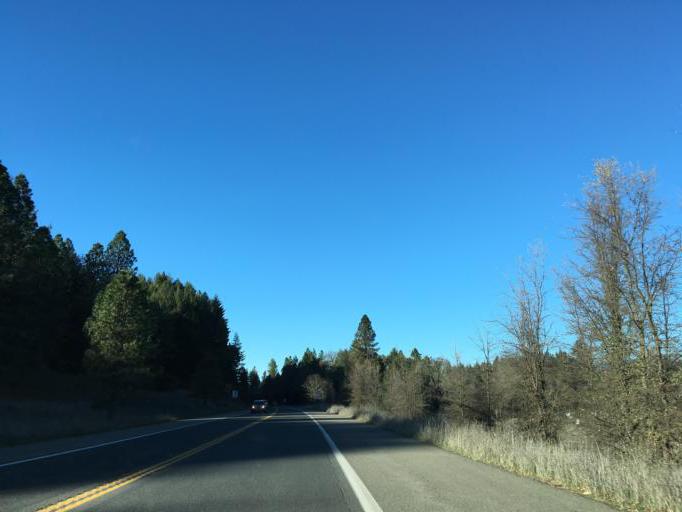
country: US
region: California
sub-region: Mendocino County
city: Laytonville
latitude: 39.7088
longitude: -123.4901
